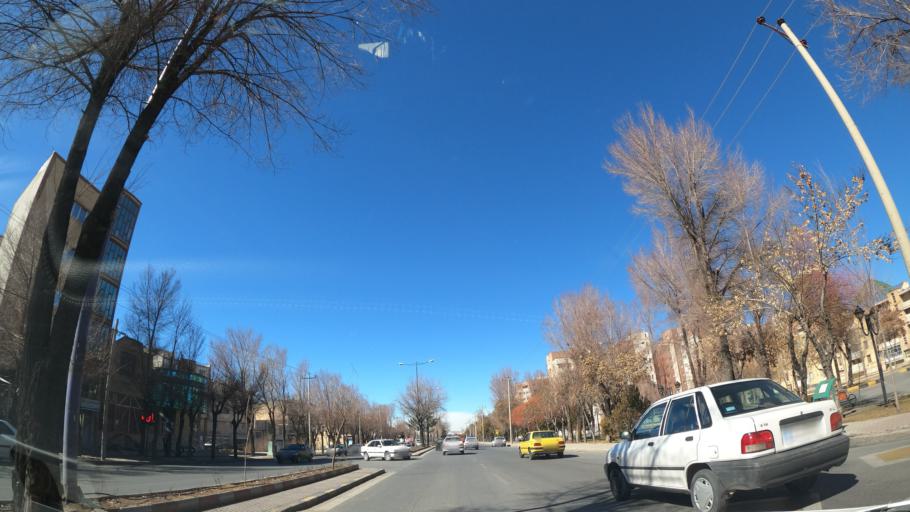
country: IR
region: Chahar Mahall va Bakhtiari
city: Shahrekord
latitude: 32.3132
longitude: 50.8786
